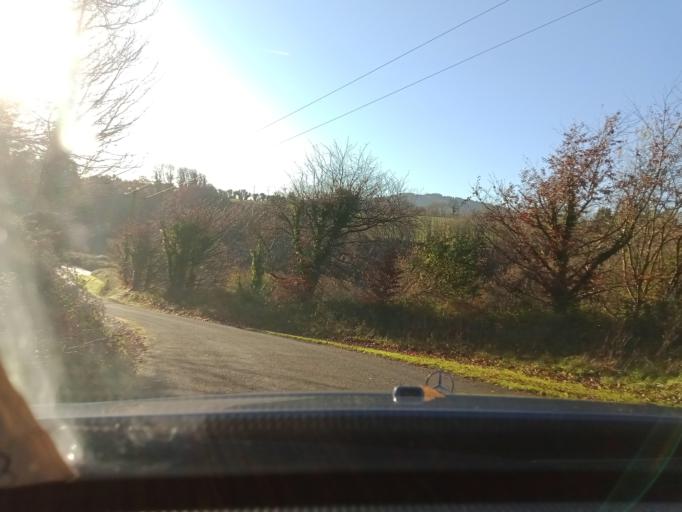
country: IE
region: Munster
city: Carrick-on-Suir
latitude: 52.4274
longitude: -7.3898
